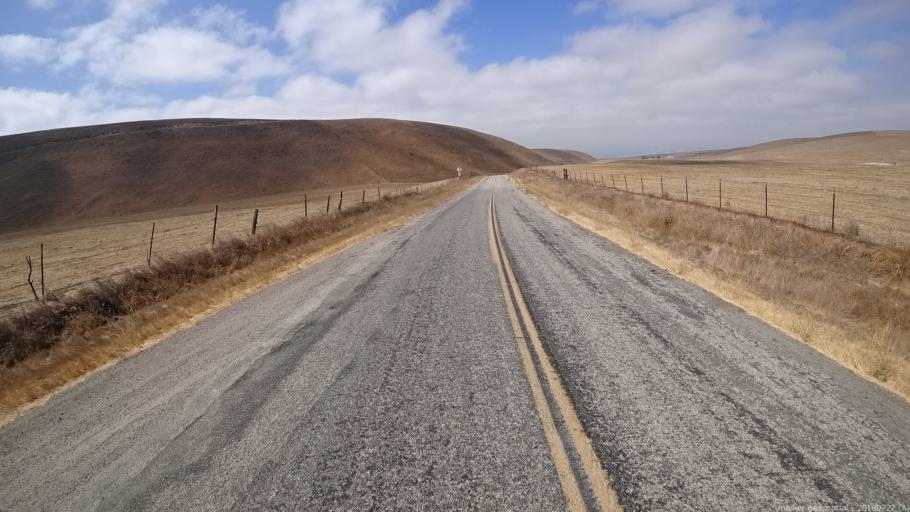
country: US
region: California
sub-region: Monterey County
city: King City
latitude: 36.2338
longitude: -121.0445
